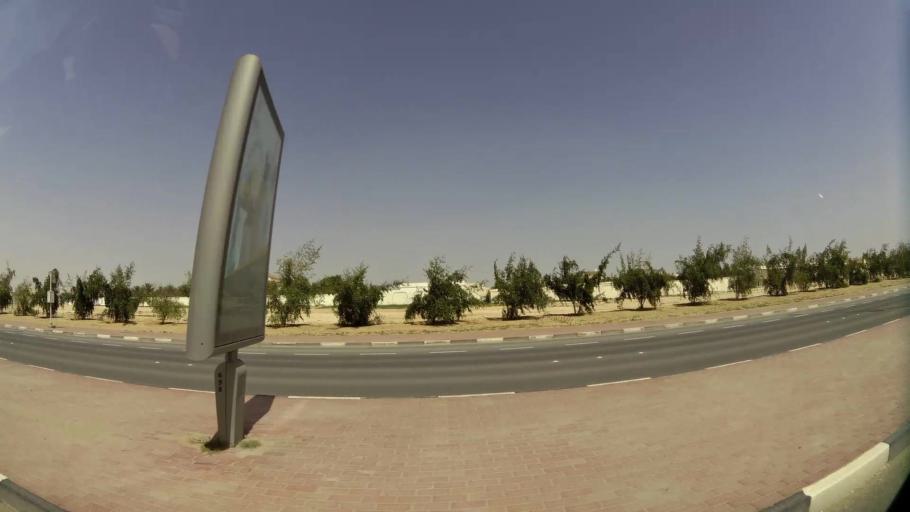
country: QA
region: Baladiyat Umm Salal
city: Umm Salal Muhammad
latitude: 25.3846
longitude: 51.4254
